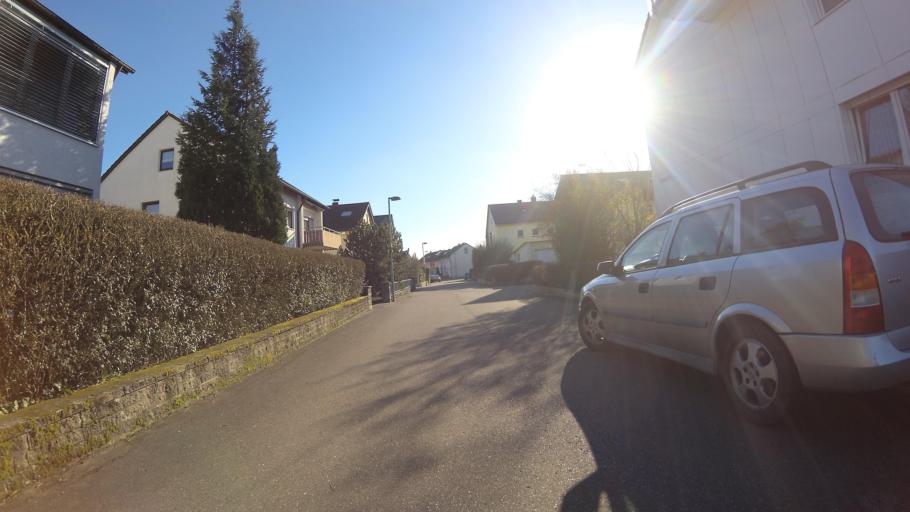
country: DE
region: Baden-Wuerttemberg
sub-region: Regierungsbezirk Stuttgart
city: Untereisesheim
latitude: 49.2380
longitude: 9.1948
